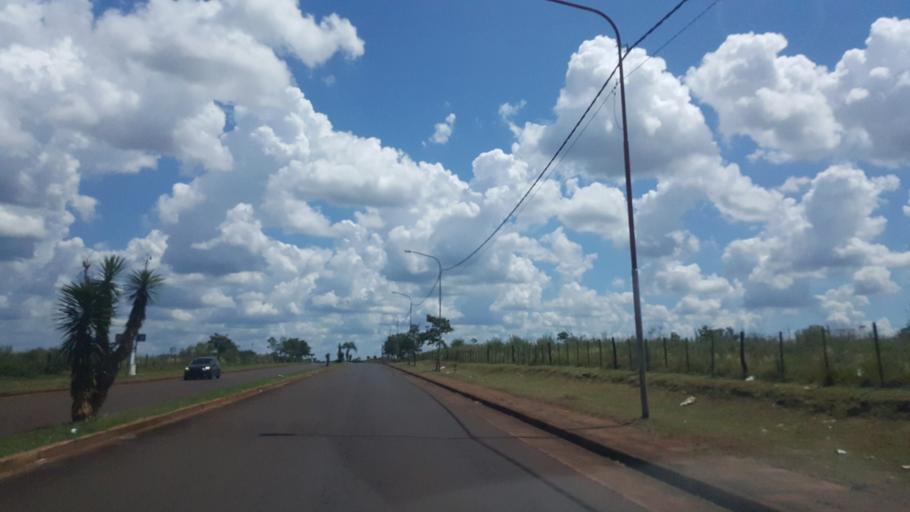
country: AR
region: Misiones
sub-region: Departamento de Capital
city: Posadas
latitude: -27.3791
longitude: -55.9622
